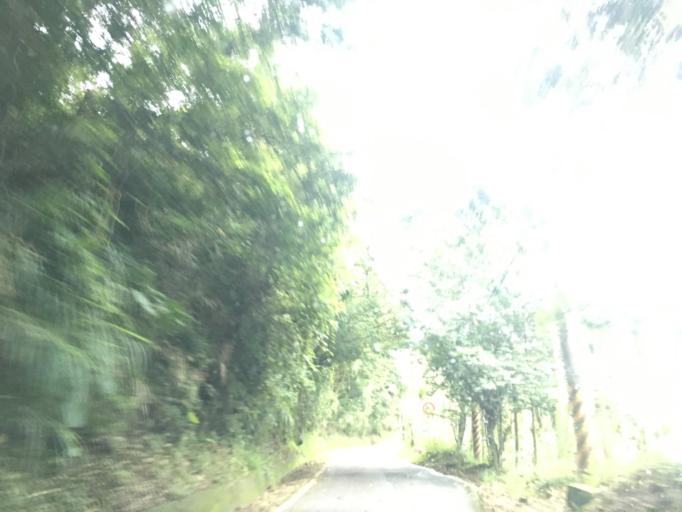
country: TW
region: Taiwan
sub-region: Yunlin
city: Douliu
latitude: 23.5651
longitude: 120.6256
